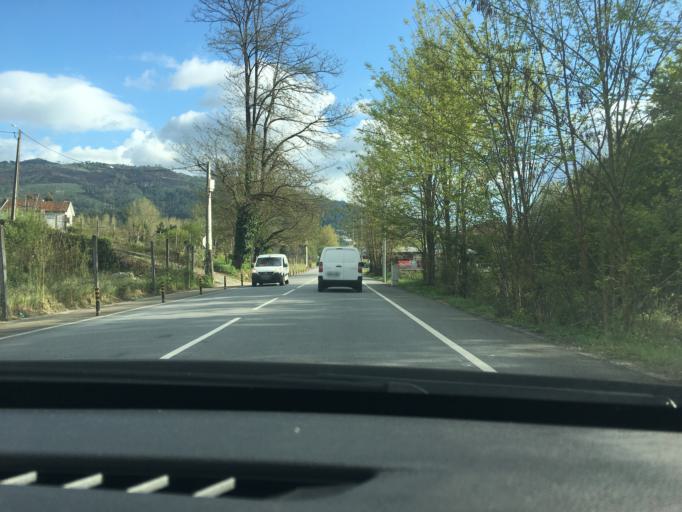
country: PT
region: Viana do Castelo
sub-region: Ponte da Barca
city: Ponte da Barca
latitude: 41.7938
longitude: -8.4143
